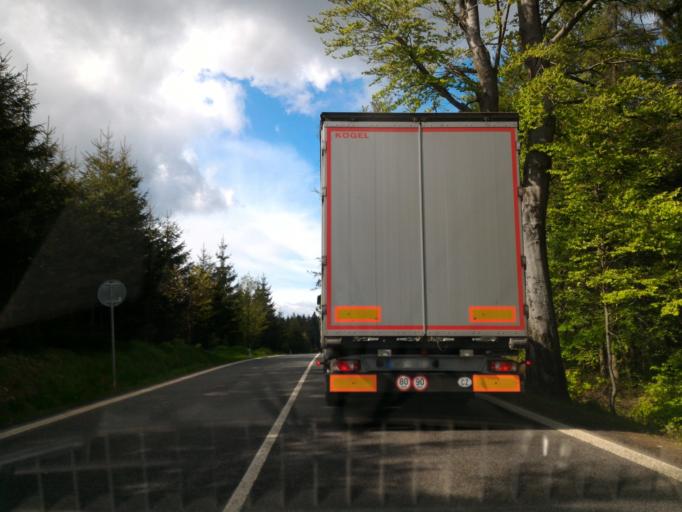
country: CZ
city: Cvikov
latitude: 50.8167
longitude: 14.5952
